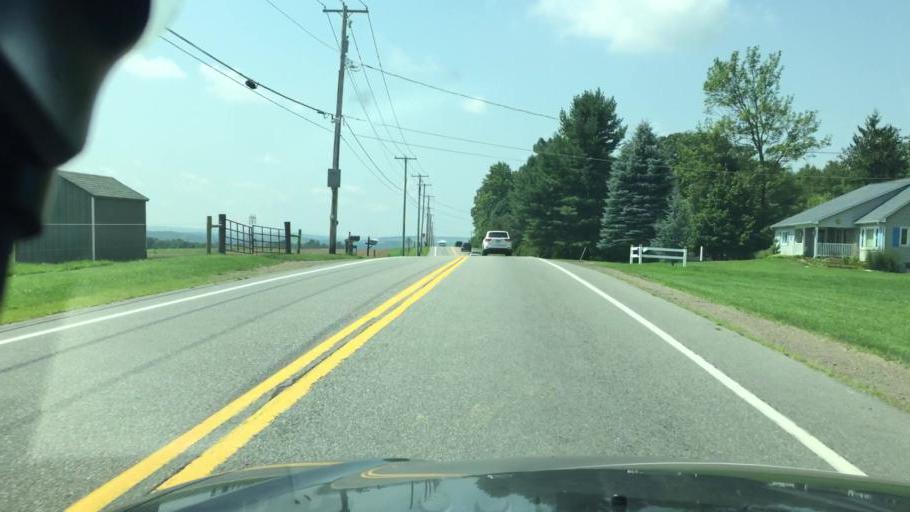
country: US
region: Pennsylvania
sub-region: Columbia County
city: Catawissa
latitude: 40.9261
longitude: -76.4613
